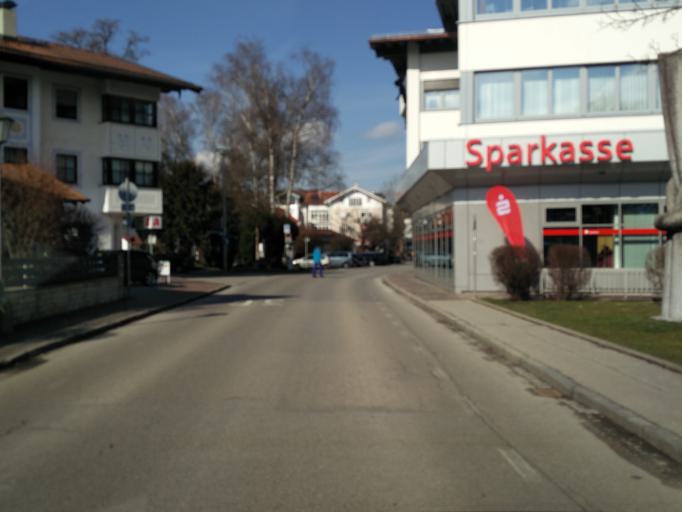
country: DE
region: Bavaria
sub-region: Upper Bavaria
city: Prien am Chiemsee
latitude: 47.8532
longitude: 12.3470
